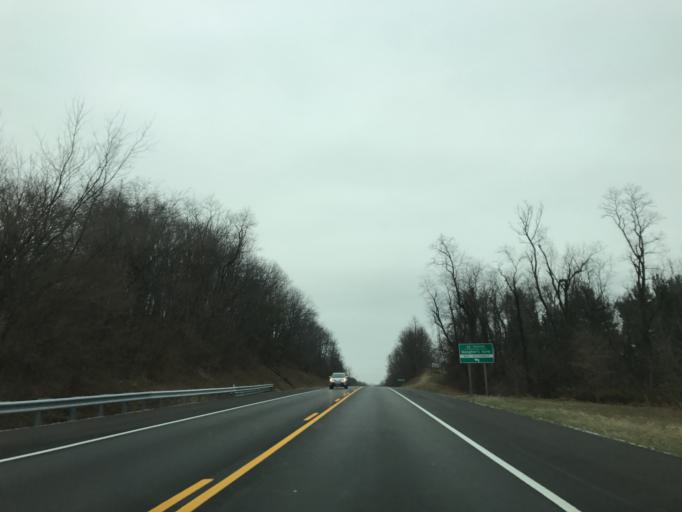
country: US
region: Maryland
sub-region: Carroll County
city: Westminster
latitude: 39.6036
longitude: -77.0552
